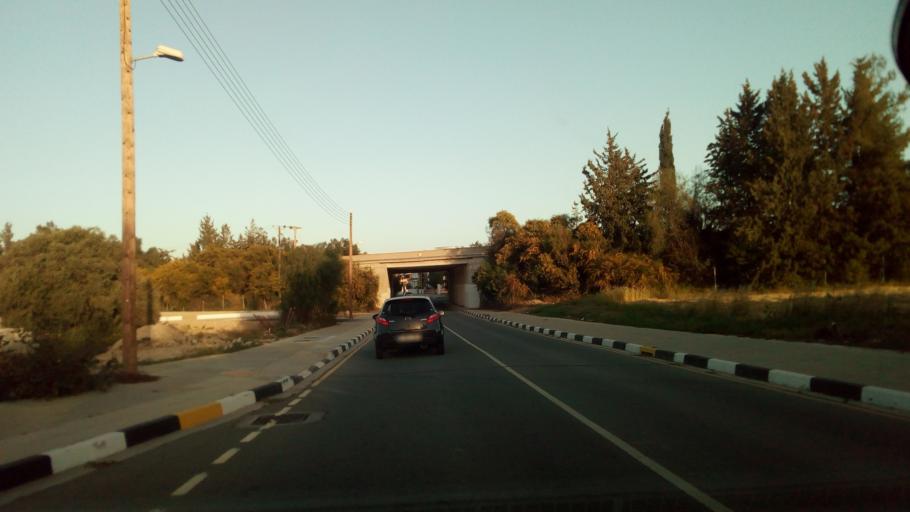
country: CY
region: Larnaka
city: Voroklini
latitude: 34.9767
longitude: 33.6641
